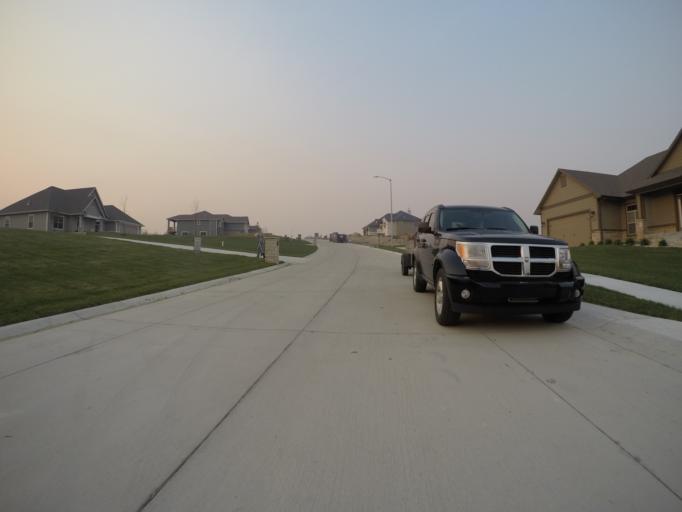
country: US
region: Kansas
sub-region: Riley County
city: Manhattan
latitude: 39.2049
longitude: -96.6533
